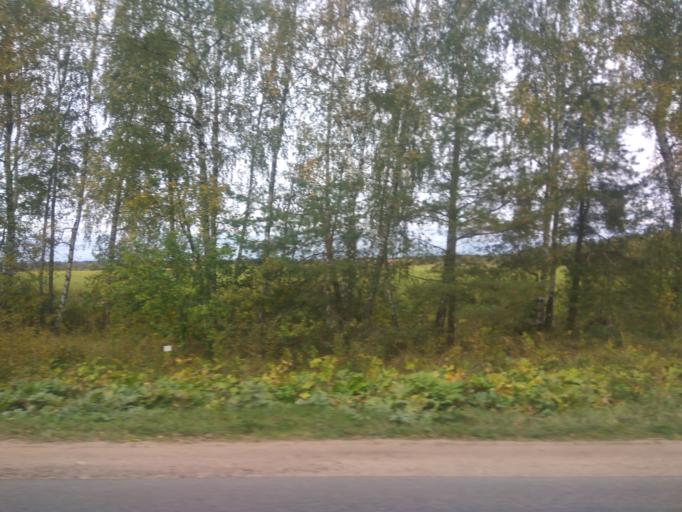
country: RU
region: Moskovskaya
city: Krasnoarmeysk
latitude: 56.0123
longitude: 38.1538
